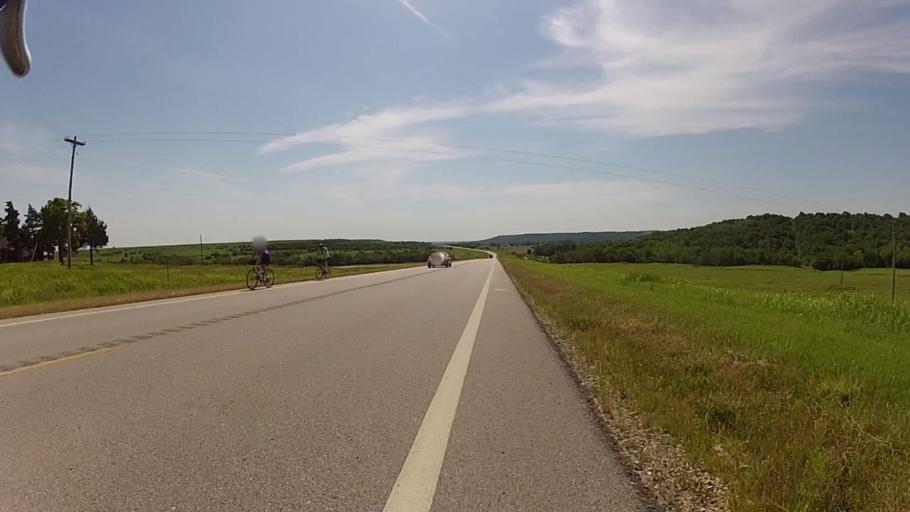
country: US
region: Kansas
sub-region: Chautauqua County
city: Sedan
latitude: 37.1105
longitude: -96.5932
